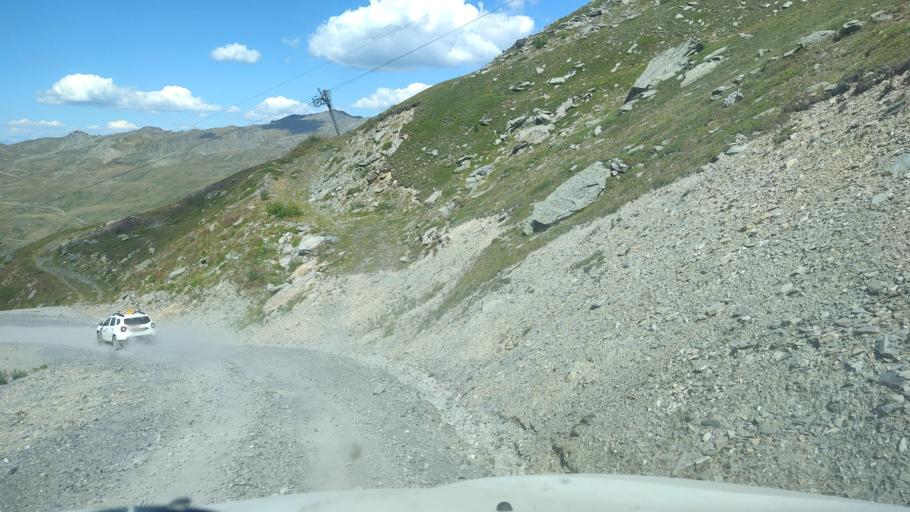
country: FR
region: Rhone-Alpes
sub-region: Departement de la Savoie
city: Val Thorens
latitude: 45.3075
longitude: 6.5175
